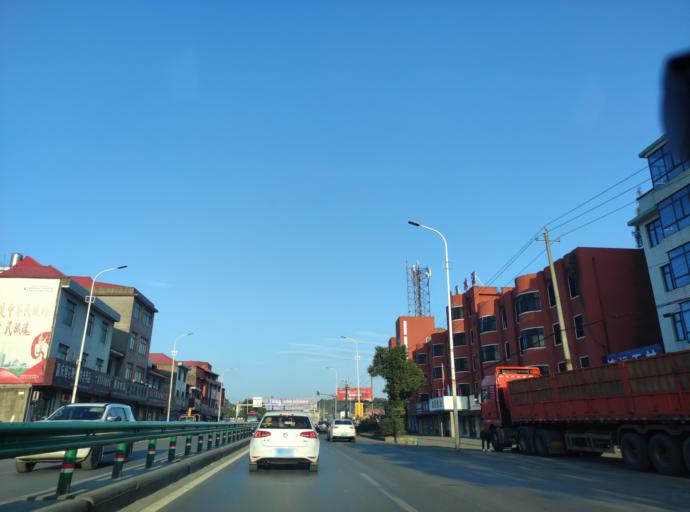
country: CN
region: Jiangxi Sheng
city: Xiangdong
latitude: 27.6497
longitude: 113.7763
